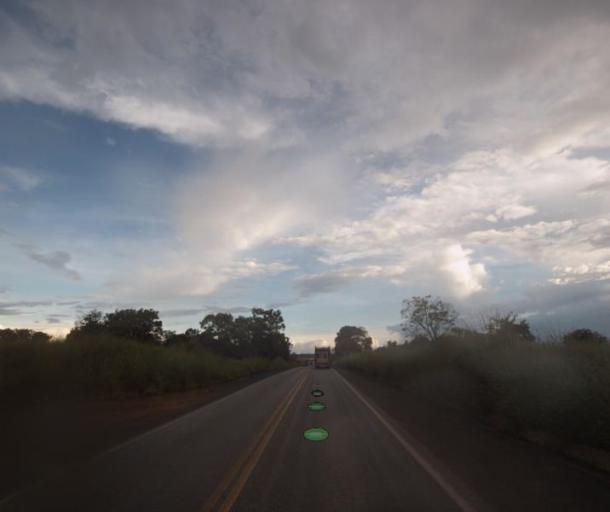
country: BR
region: Goias
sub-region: Uruacu
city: Uruacu
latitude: -13.9875
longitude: -49.0906
